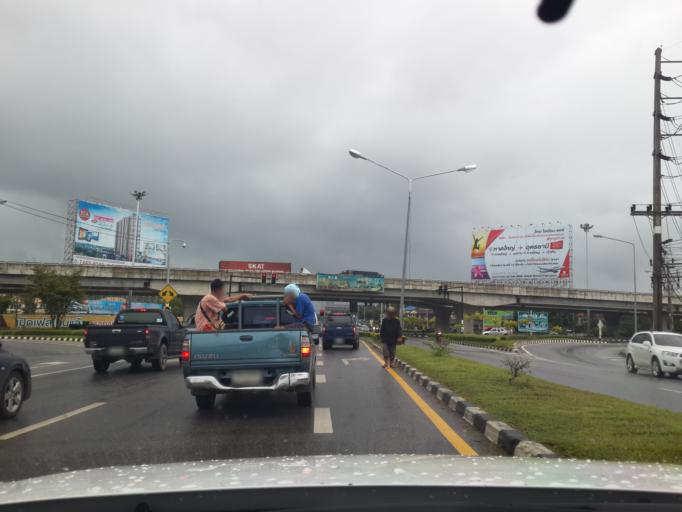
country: TH
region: Songkhla
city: Hat Yai
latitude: 6.9861
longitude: 100.4283
